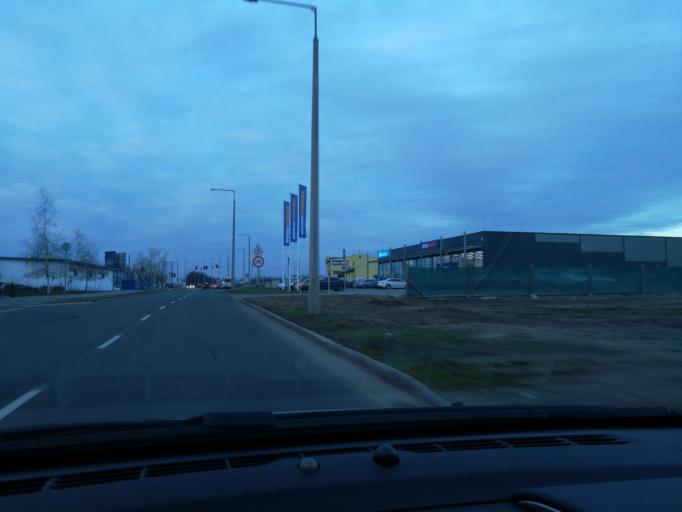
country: HU
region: Szabolcs-Szatmar-Bereg
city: Nyiregyhaza
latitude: 47.9685
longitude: 21.7415
